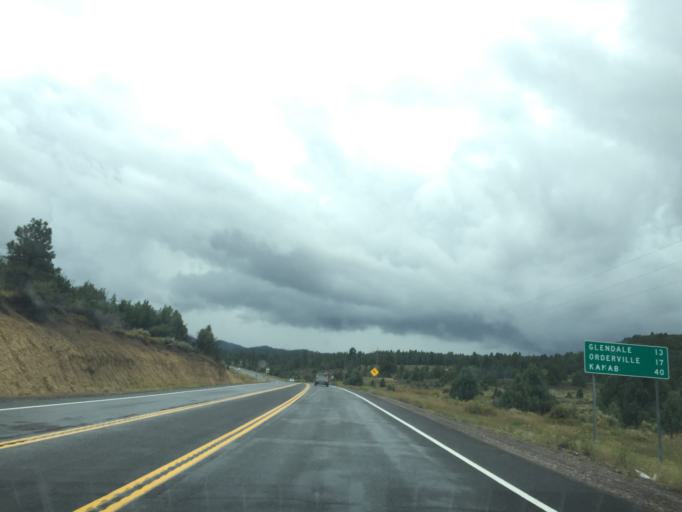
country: US
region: Utah
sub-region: Garfield County
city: Panguitch
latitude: 37.4862
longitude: -112.5138
